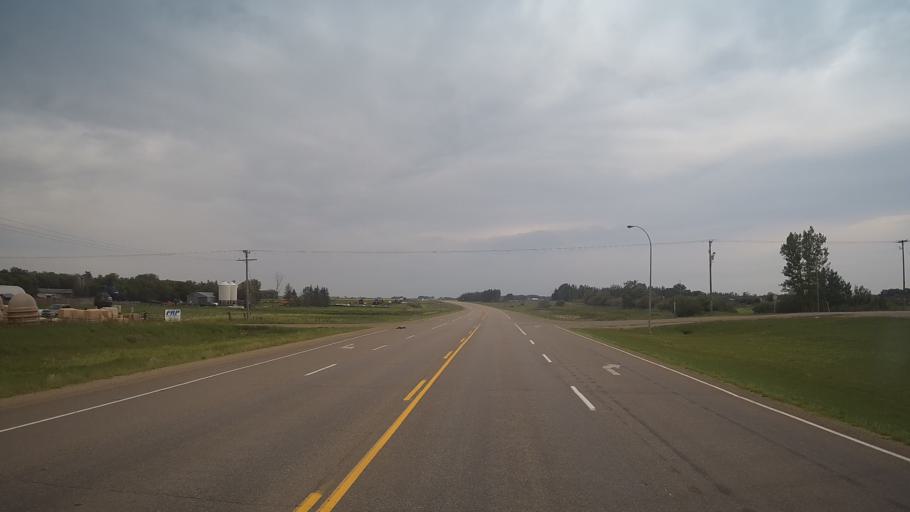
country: CA
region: Saskatchewan
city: Langham
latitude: 52.1289
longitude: -107.2281
